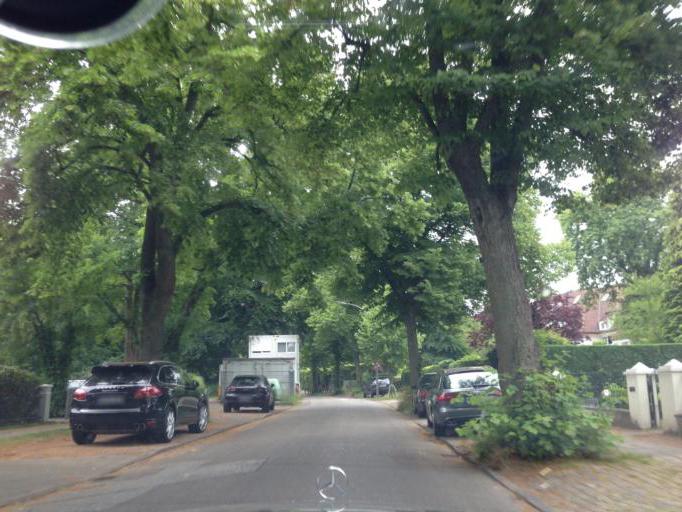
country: DE
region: Hamburg
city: Wandsbek
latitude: 53.5649
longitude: 10.0924
